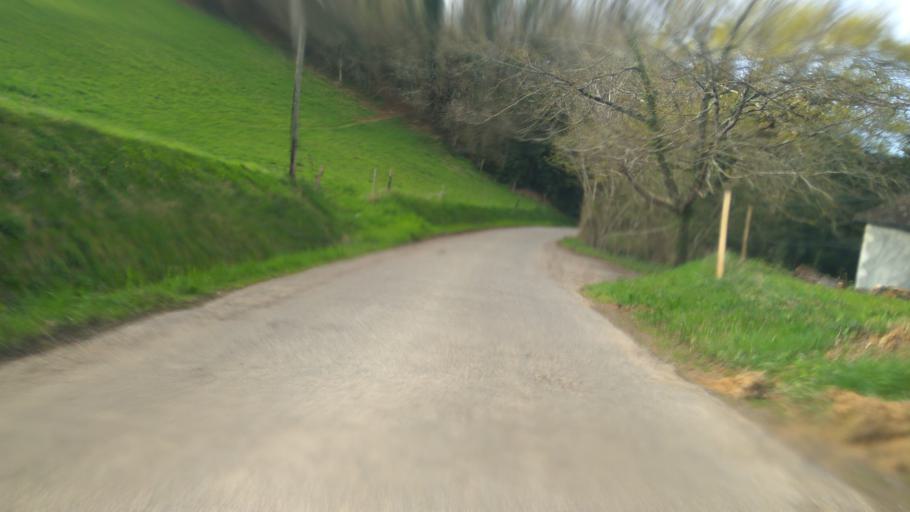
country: FR
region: Aquitaine
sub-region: Departement des Pyrenees-Atlantiques
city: Mazeres-Lezons
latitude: 43.2634
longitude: -0.3559
